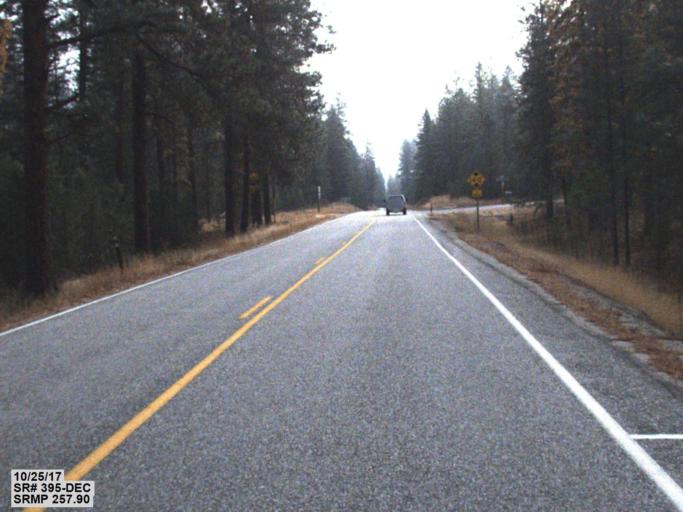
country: US
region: Washington
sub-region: Stevens County
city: Kettle Falls
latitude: 48.8371
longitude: -118.1884
